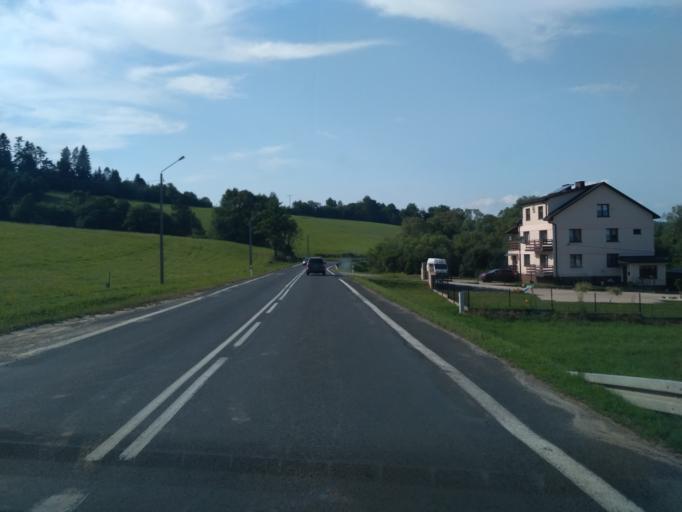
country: PL
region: Subcarpathian Voivodeship
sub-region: Powiat leski
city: Olszanica
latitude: 49.4468
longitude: 22.4812
